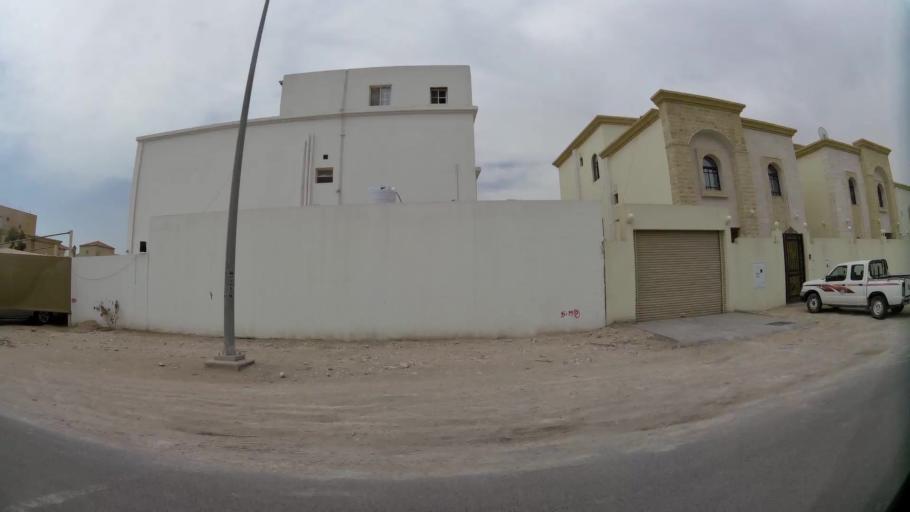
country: QA
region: Baladiyat ad Dawhah
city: Doha
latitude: 25.2212
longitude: 51.4735
